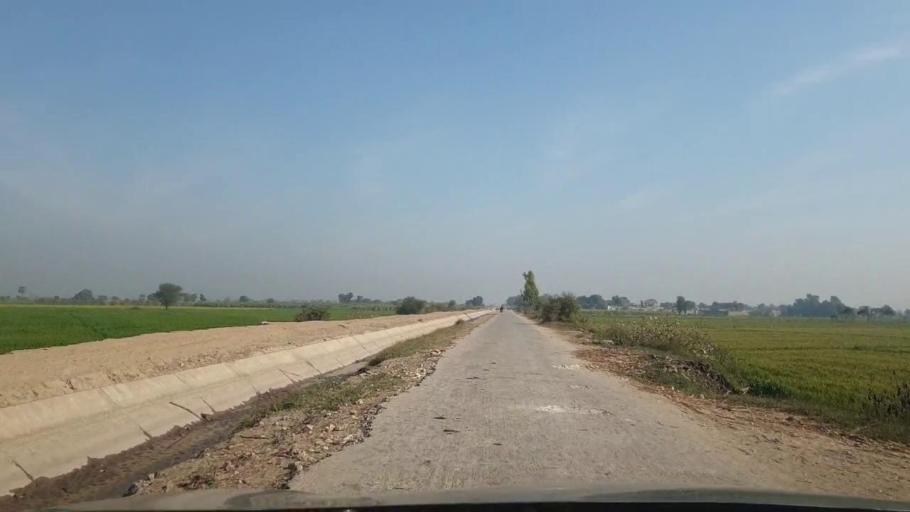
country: PK
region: Sindh
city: Tando Allahyar
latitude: 25.5892
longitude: 68.7154
